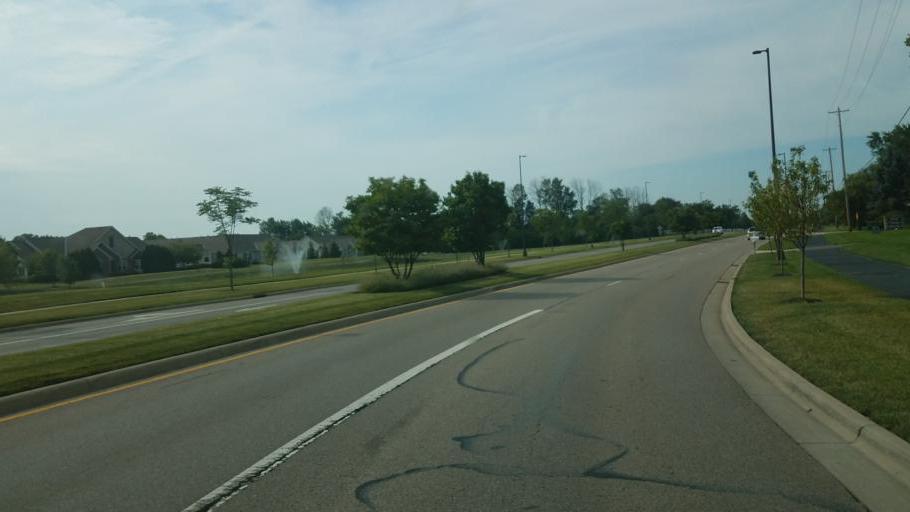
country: US
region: Ohio
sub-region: Franklin County
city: Dublin
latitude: 40.0912
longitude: -83.1585
